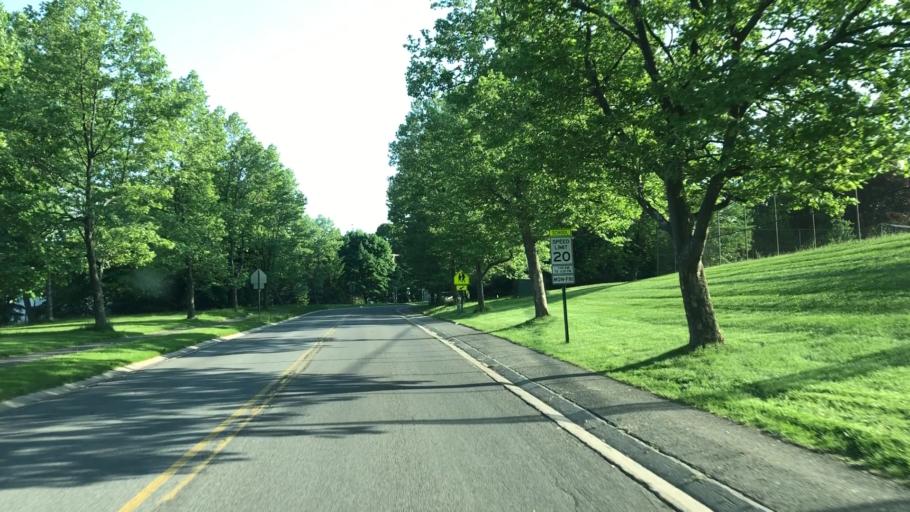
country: US
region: New York
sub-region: Wayne County
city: Macedon
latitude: 43.1234
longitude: -77.3064
